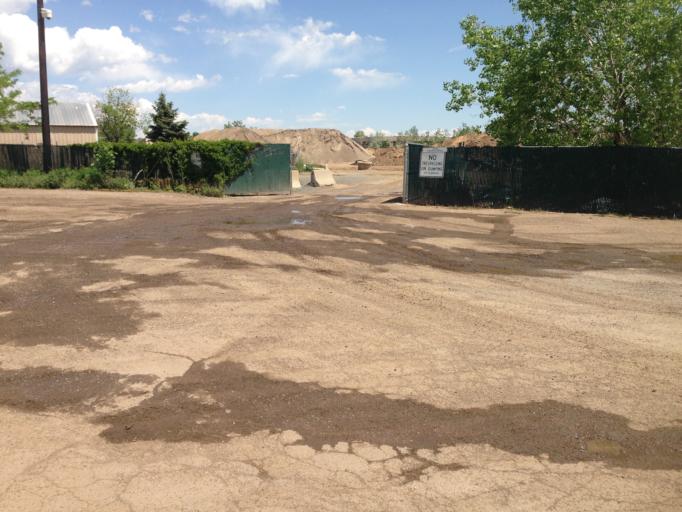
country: US
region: Colorado
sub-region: Boulder County
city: Boulder
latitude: 40.0249
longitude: -105.2303
